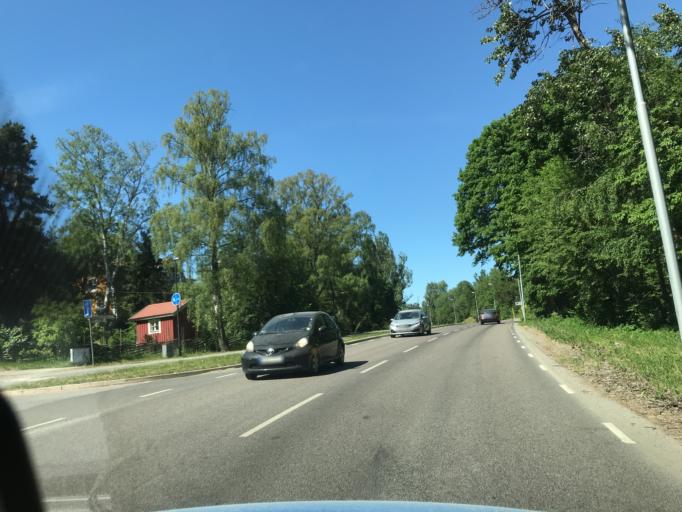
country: SE
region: Stockholm
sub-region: Stockholms Kommun
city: Kista
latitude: 59.4068
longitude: 17.9756
